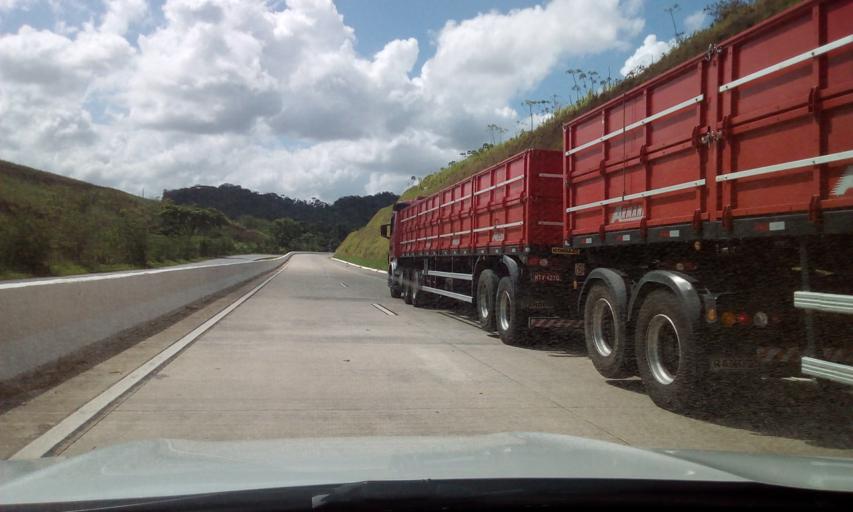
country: BR
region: Pernambuco
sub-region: Palmares
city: Palmares
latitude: -8.7528
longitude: -35.6025
